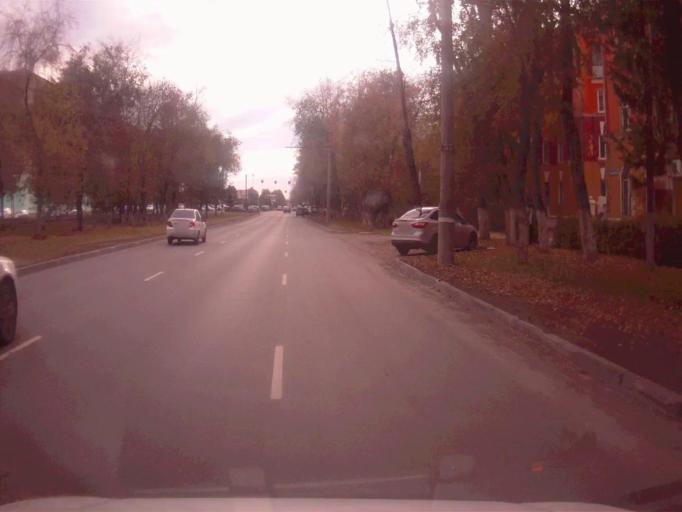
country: RU
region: Chelyabinsk
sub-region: Gorod Chelyabinsk
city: Chelyabinsk
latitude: 55.1196
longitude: 61.4717
